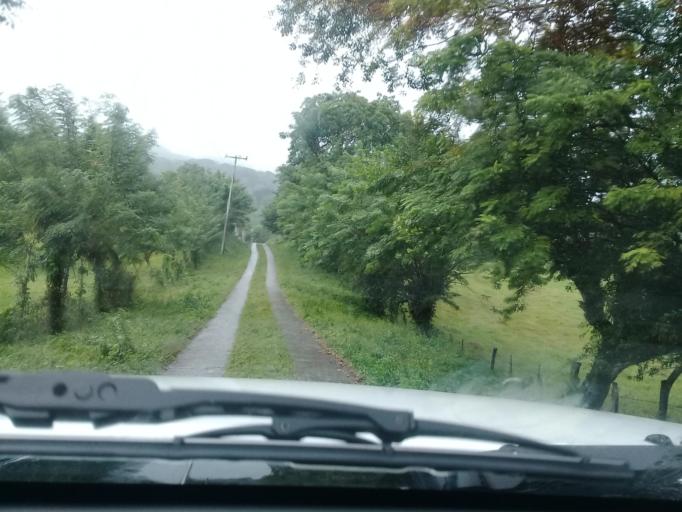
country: MX
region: Veracruz
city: Santiago Tuxtla
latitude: 18.4619
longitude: -95.3226
